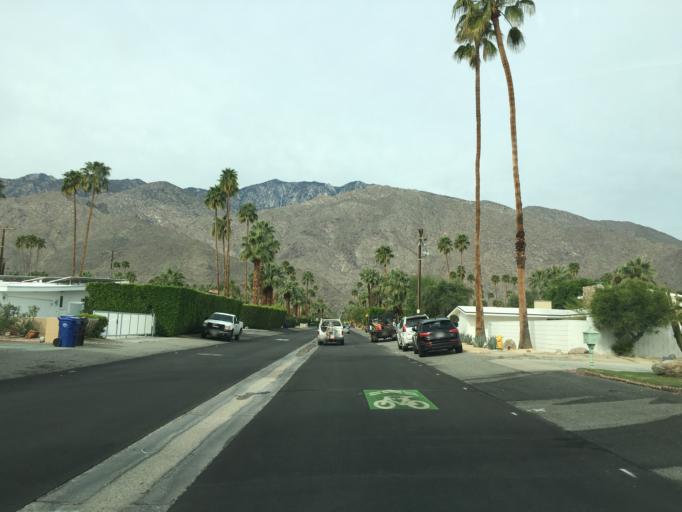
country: US
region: California
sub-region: Riverside County
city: Palm Springs
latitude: 33.8087
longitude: -116.5318
